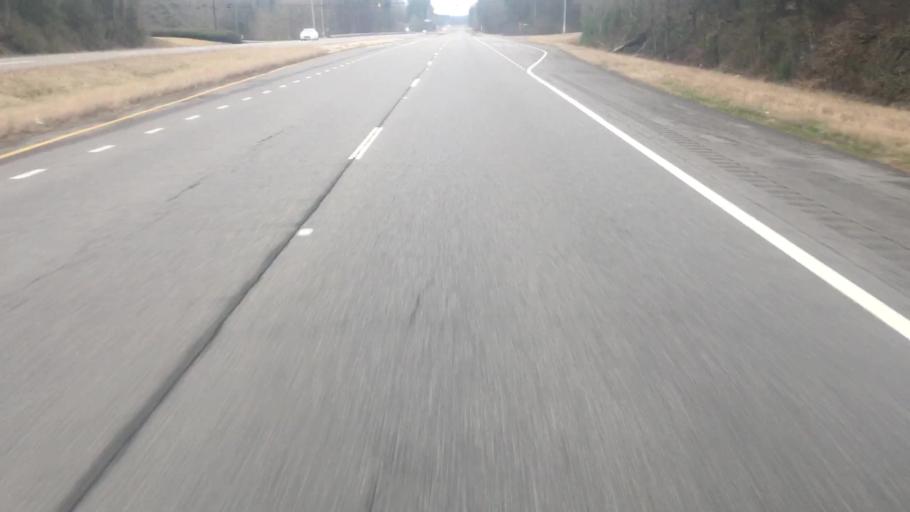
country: US
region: Alabama
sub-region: Walker County
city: Cordova
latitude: 33.8212
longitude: -87.1831
